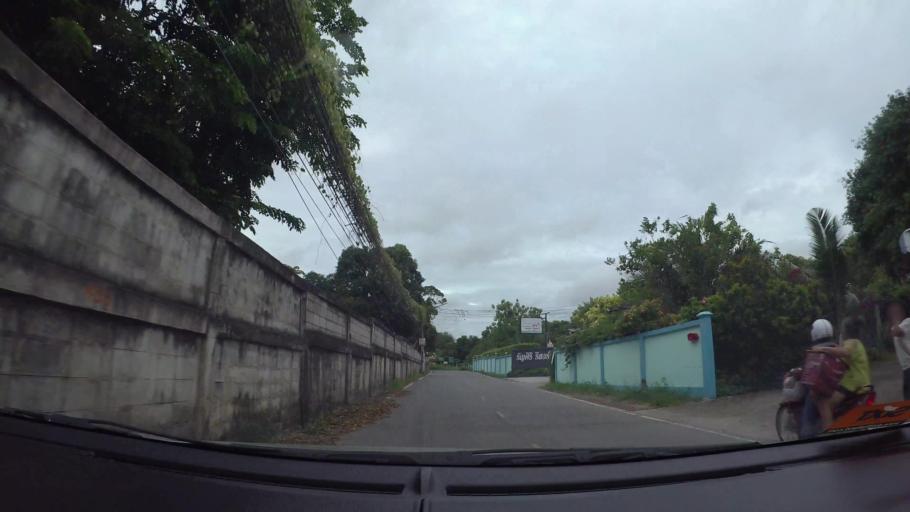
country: TH
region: Chon Buri
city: Sattahip
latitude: 12.6884
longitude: 100.8965
